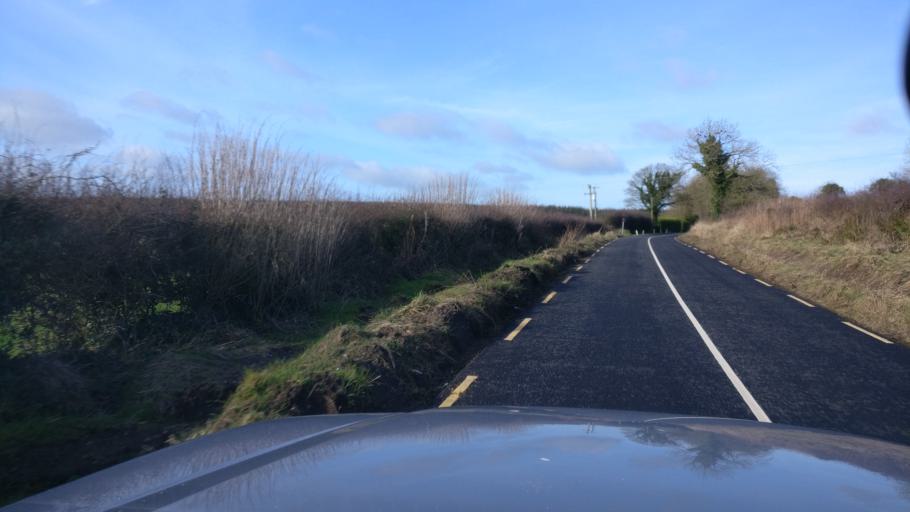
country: IE
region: Leinster
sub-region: Kilkenny
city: Castlecomer
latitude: 52.9057
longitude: -7.1821
